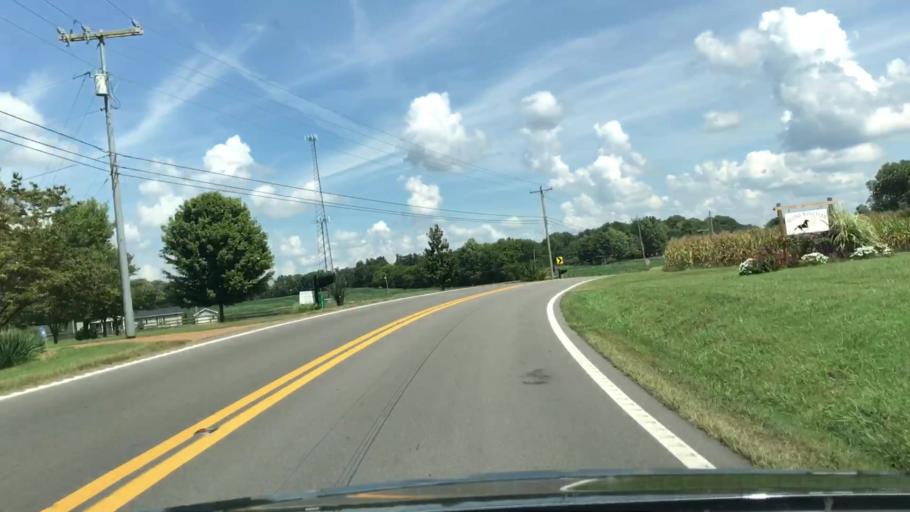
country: US
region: Tennessee
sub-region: Sumner County
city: Portland
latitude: 36.5431
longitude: -86.5215
